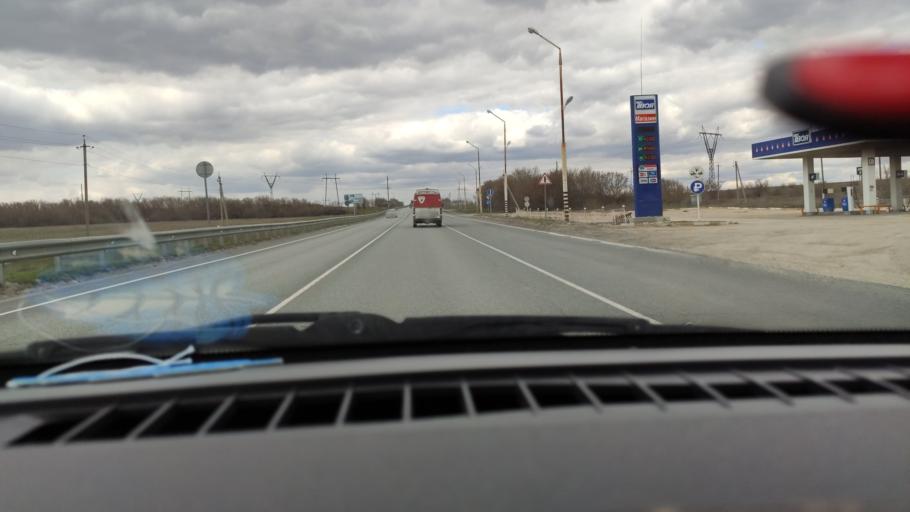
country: RU
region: Saratov
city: Tersa
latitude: 52.0998
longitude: 47.5182
